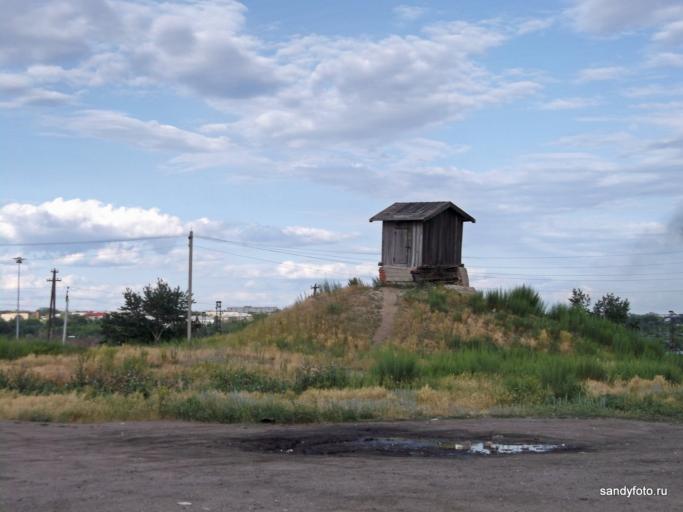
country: RU
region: Chelyabinsk
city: Troitsk
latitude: 54.0461
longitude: 61.6062
